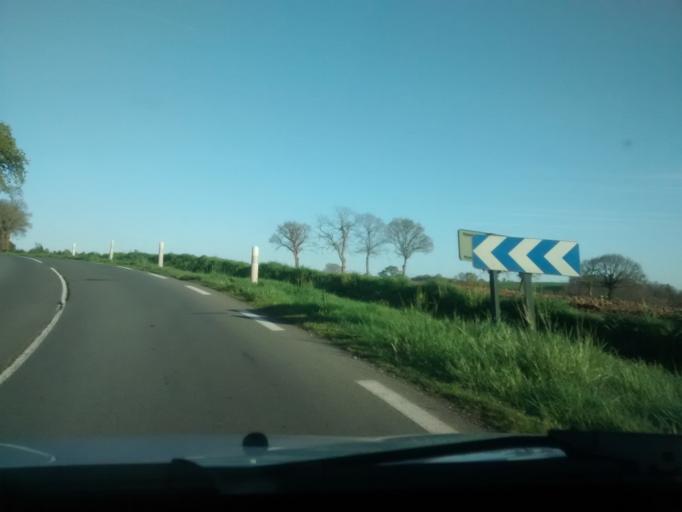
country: FR
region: Brittany
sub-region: Departement d'Ille-et-Vilaine
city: Pleine-Fougeres
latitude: 48.4913
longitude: -1.5747
